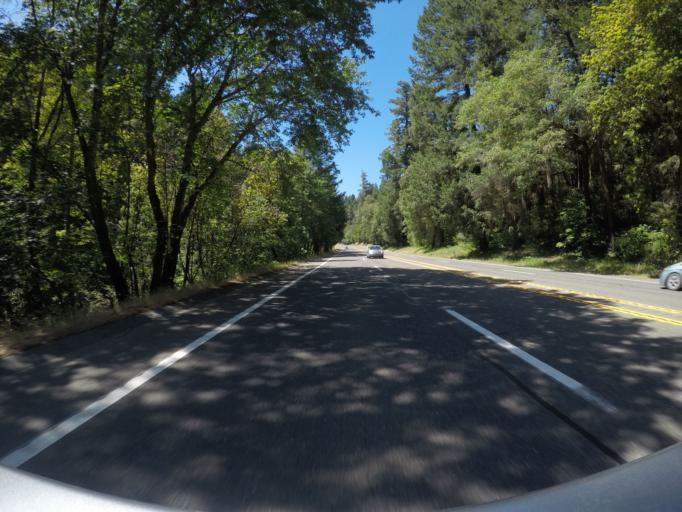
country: US
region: California
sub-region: Mendocino County
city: Laytonville
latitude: 39.5767
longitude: -123.4397
